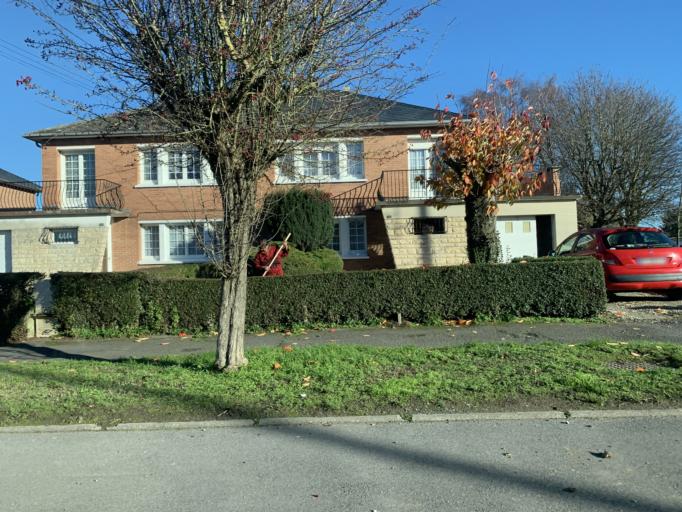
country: FR
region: Nord-Pas-de-Calais
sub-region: Departement du Nord
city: Cambrai
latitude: 50.1690
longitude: 3.2622
